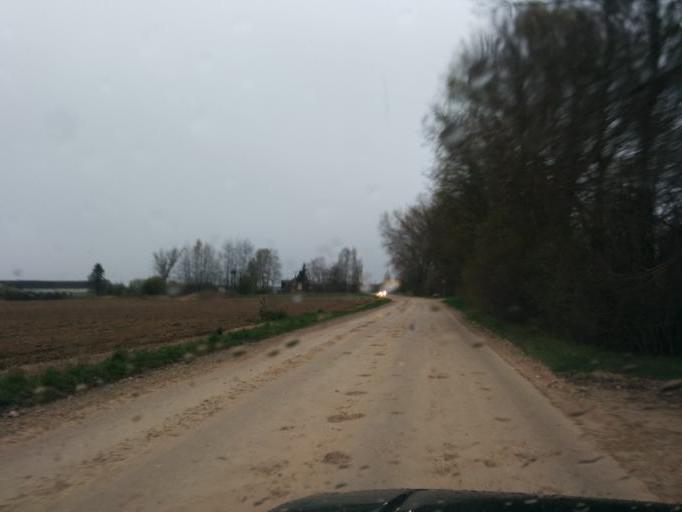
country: LV
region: Lecava
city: Iecava
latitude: 56.6050
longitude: 24.1836
